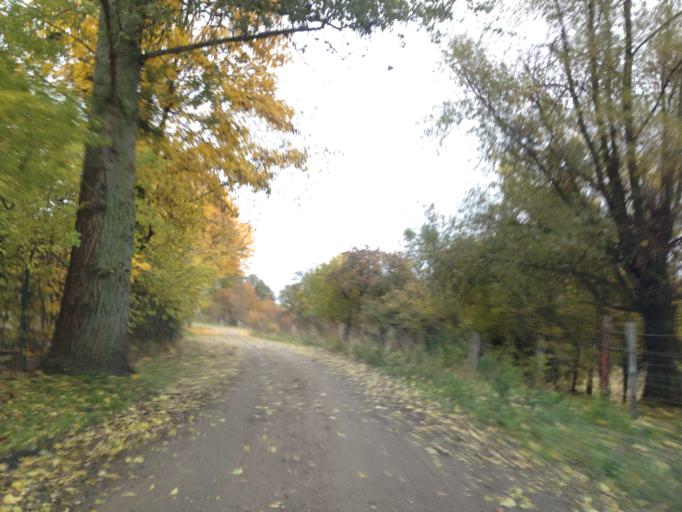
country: PL
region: Pomeranian Voivodeship
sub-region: Powiat kwidzynski
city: Prabuty
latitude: 53.7356
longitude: 19.2156
